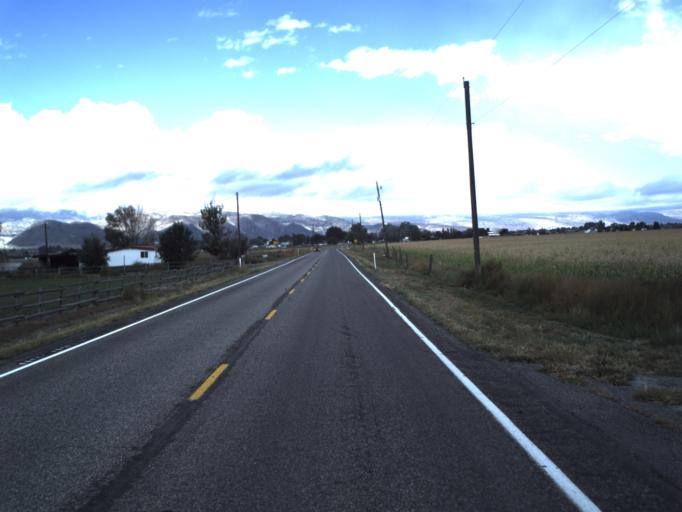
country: US
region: Utah
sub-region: Sevier County
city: Monroe
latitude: 38.6600
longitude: -112.1215
